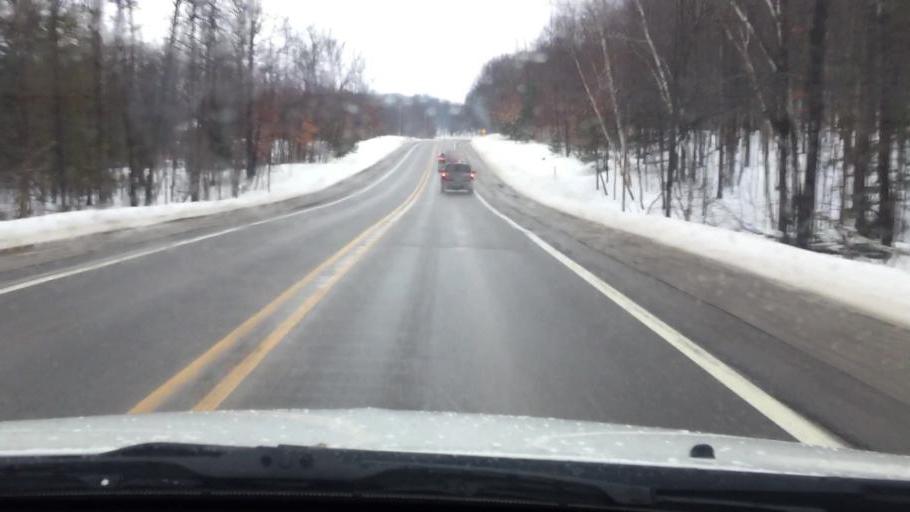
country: US
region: Michigan
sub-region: Charlevoix County
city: East Jordan
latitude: 45.2241
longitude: -85.1782
